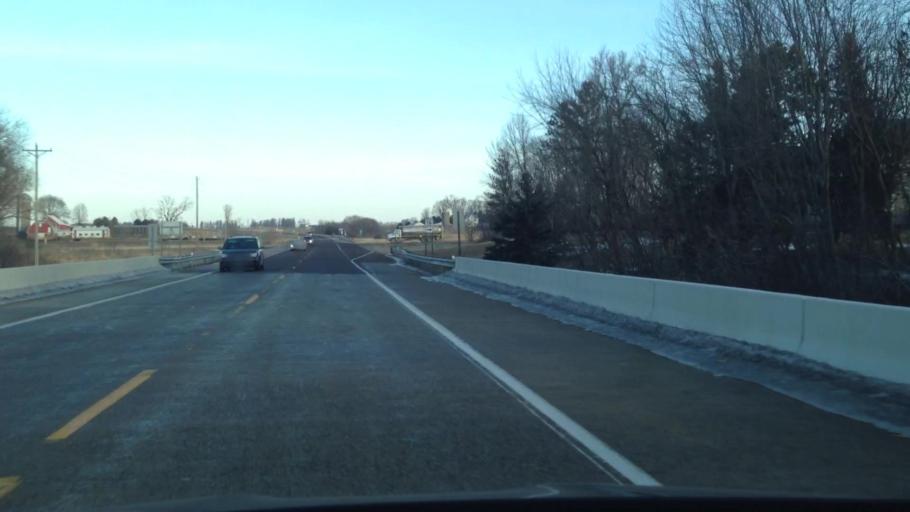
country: US
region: Minnesota
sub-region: Goodhue County
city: Goodhue
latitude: 44.3671
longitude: -92.6137
